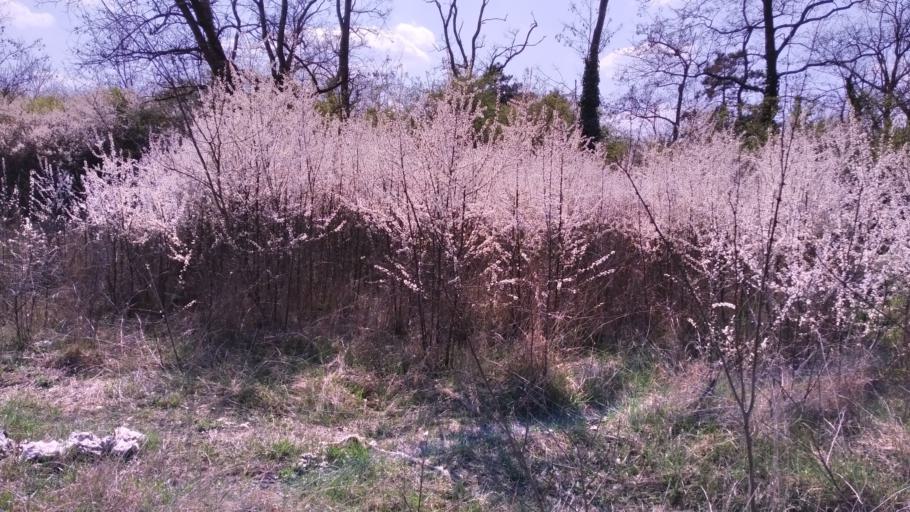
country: HU
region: Pest
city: Budakalasz
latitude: 47.6138
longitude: 19.0448
